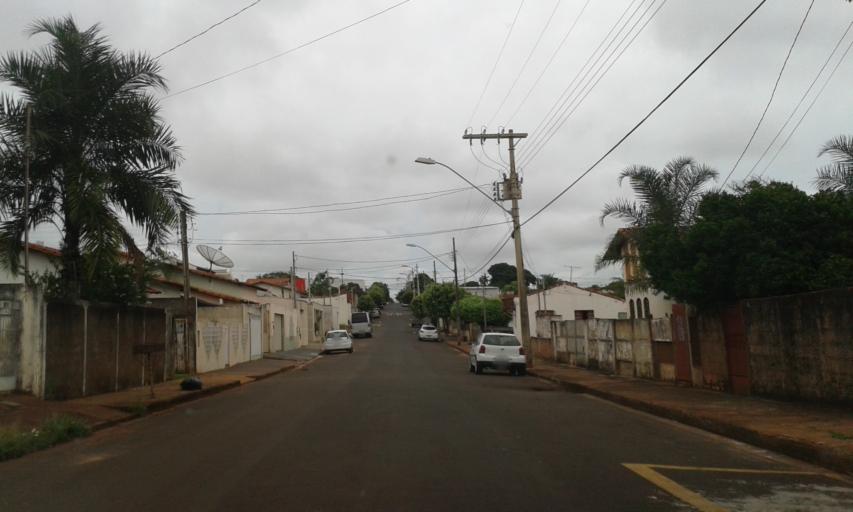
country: BR
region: Minas Gerais
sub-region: Ituiutaba
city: Ituiutaba
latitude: -18.9785
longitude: -49.4506
